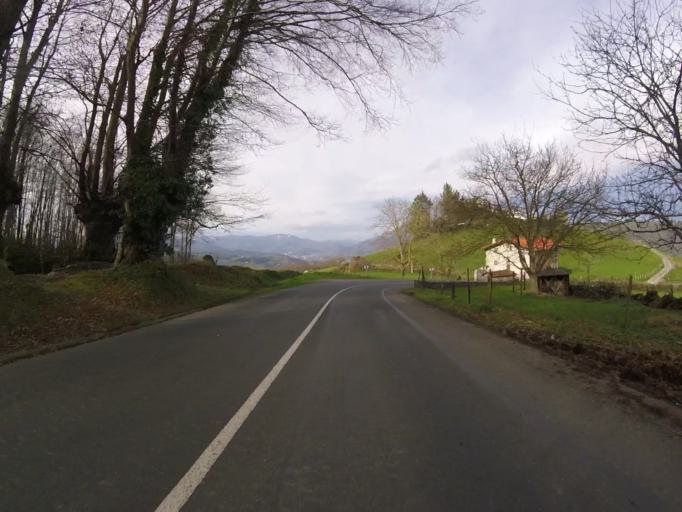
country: ES
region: Basque Country
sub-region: Provincia de Guipuzcoa
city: Beizama
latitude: 43.1653
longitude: -2.2215
